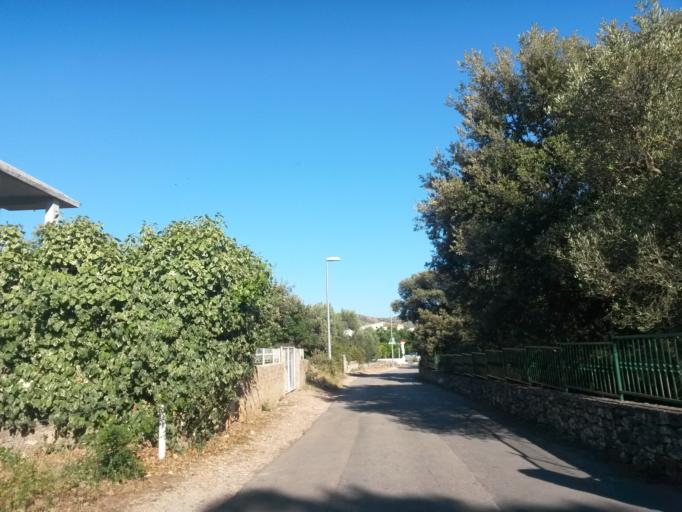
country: HR
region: Sibensko-Kniniska
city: Rogoznica
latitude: 43.5420
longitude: 15.9603
